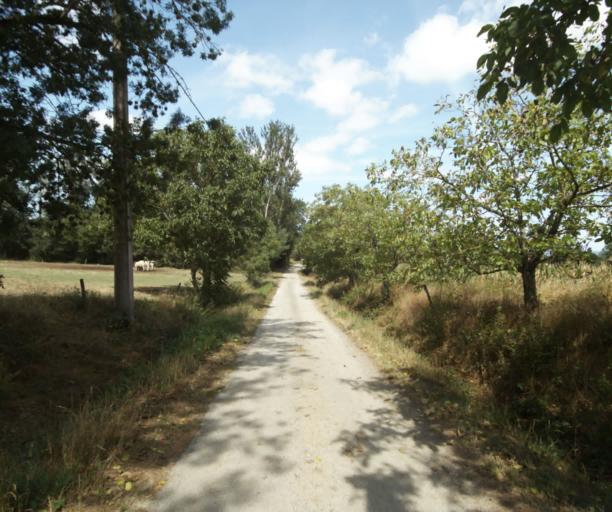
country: FR
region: Midi-Pyrenees
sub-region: Departement du Tarn
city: Soreze
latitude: 43.4804
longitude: 2.0816
